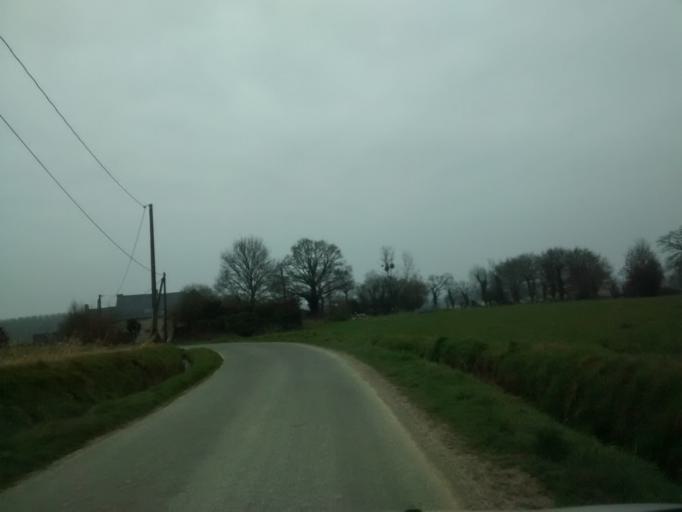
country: FR
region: Brittany
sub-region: Departement d'Ille-et-Vilaine
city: Sens-de-Bretagne
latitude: 48.3852
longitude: -1.5318
